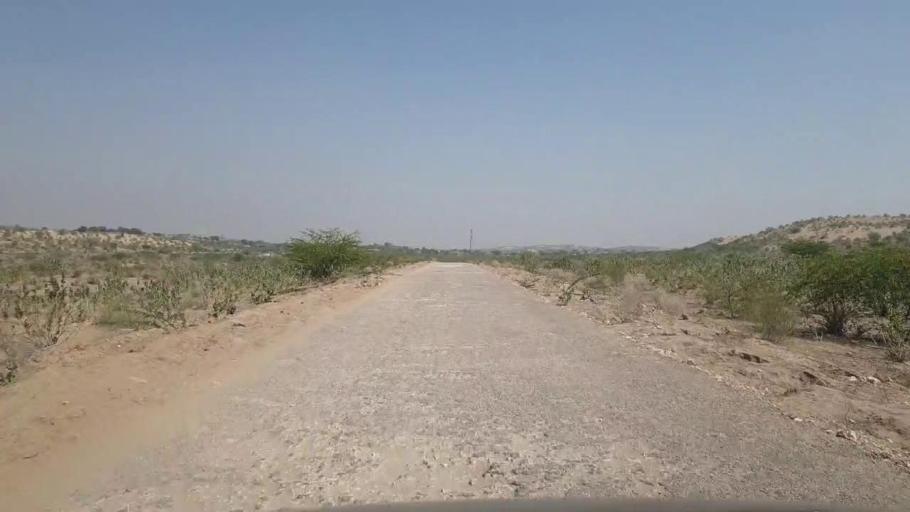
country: PK
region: Sindh
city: Chor
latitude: 25.6904
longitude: 70.1874
